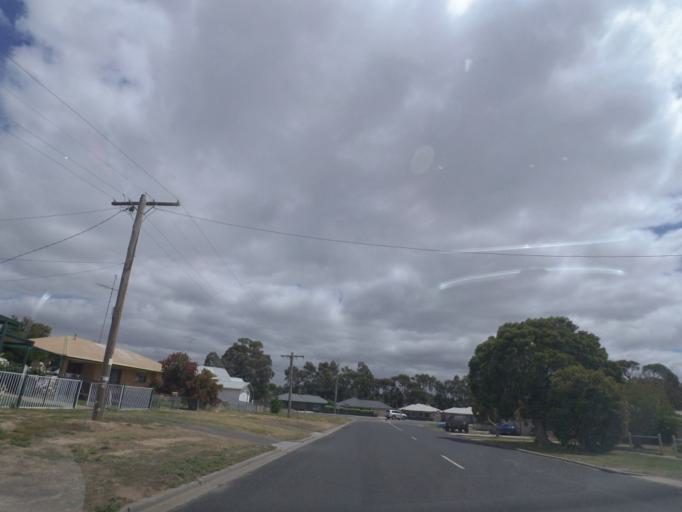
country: AU
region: Victoria
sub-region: Whittlesea
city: Whittlesea
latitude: -37.2083
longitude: 145.0447
